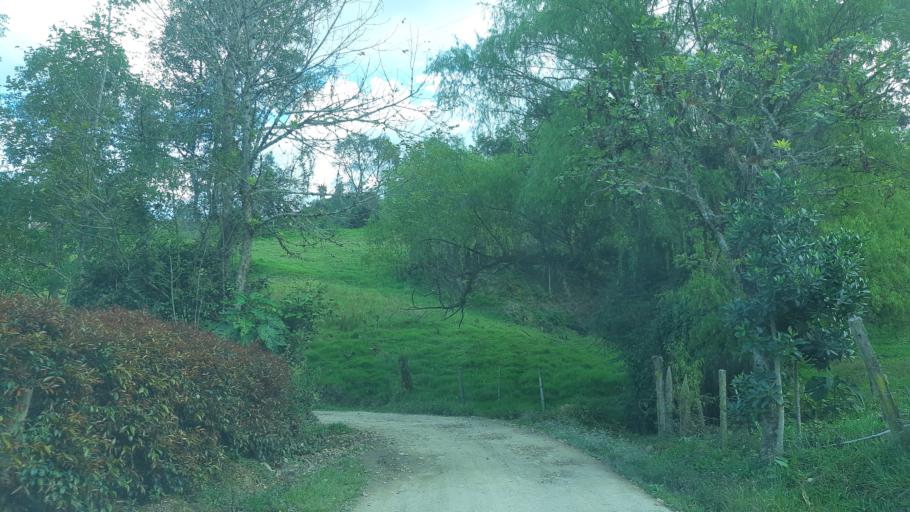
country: CO
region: Cundinamarca
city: Macheta
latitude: 5.0699
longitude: -73.6302
